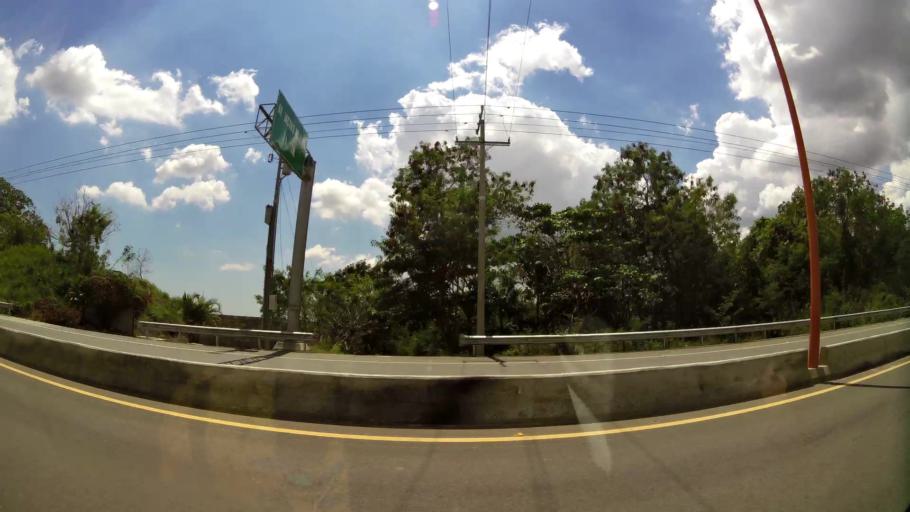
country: DO
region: Nacional
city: Santo Domingo
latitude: 18.5444
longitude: -69.9631
